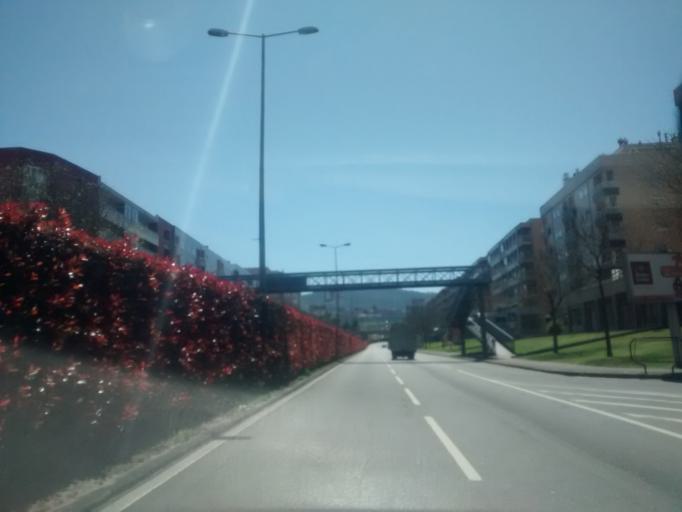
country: PT
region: Braga
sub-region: Braga
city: Braga
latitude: 41.5454
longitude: -8.4047
